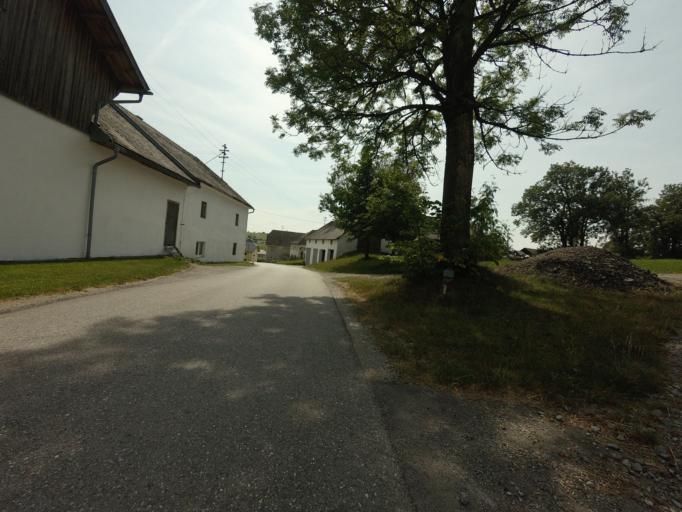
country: AT
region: Upper Austria
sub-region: Politischer Bezirk Urfahr-Umgebung
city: Schenkenfelden
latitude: 48.5210
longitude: 14.3599
